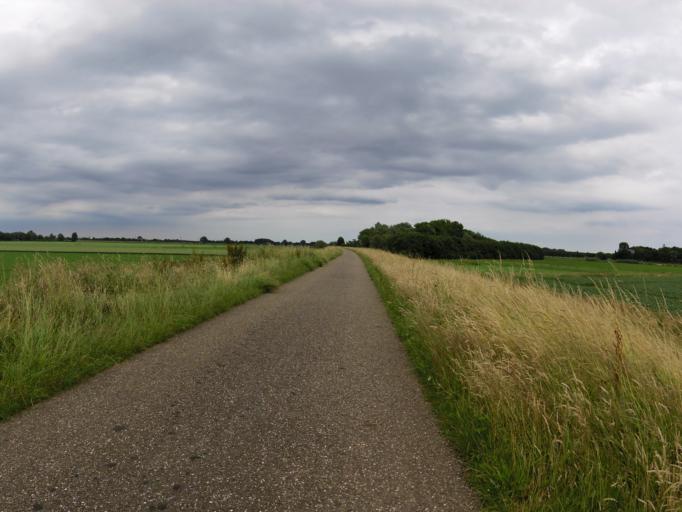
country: NL
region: North Brabant
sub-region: Gemeente Landerd
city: Reek
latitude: 51.7635
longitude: 5.7031
